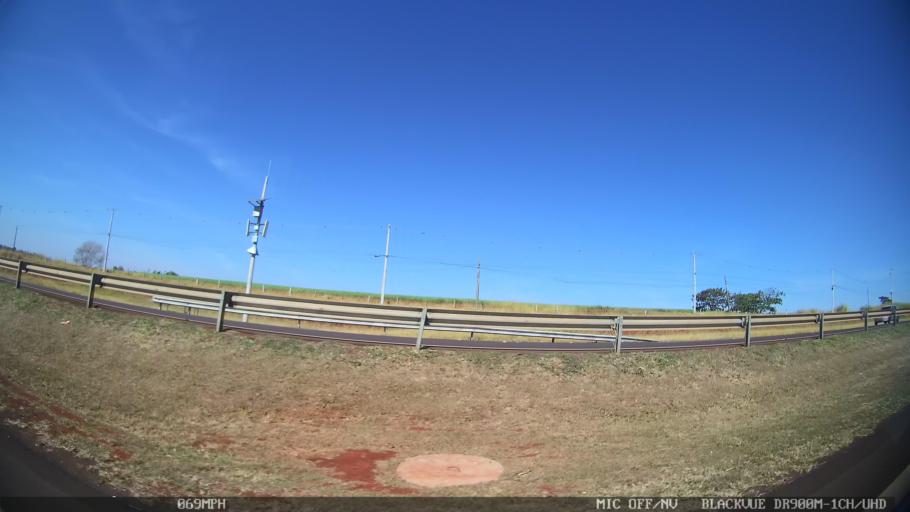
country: BR
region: Sao Paulo
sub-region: Ribeirao Preto
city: Ribeirao Preto
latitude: -21.1448
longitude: -47.8753
